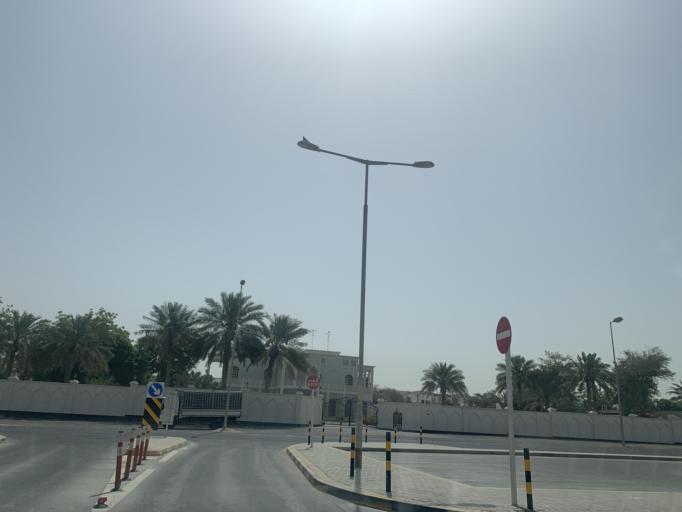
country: BH
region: Northern
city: Madinat `Isa
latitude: 26.1532
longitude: 50.5284
